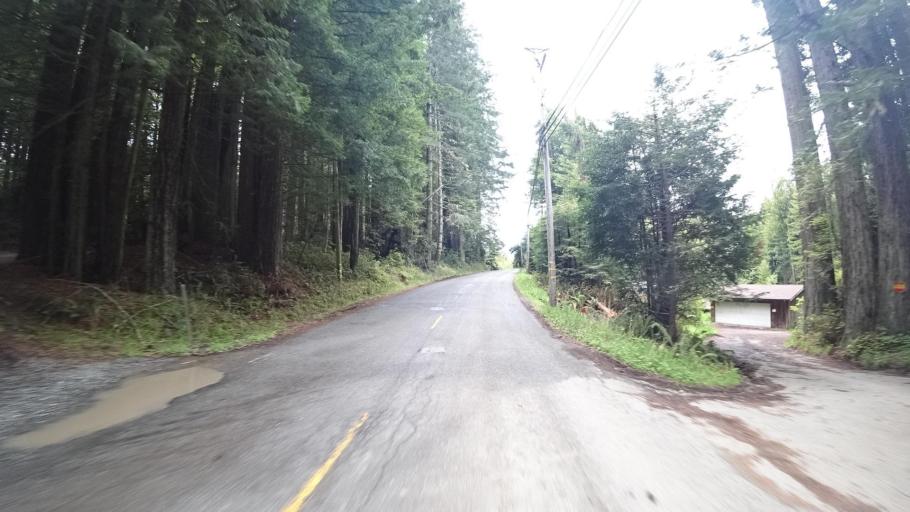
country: US
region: California
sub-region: Humboldt County
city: Bayside
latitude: 40.7995
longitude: -124.0376
